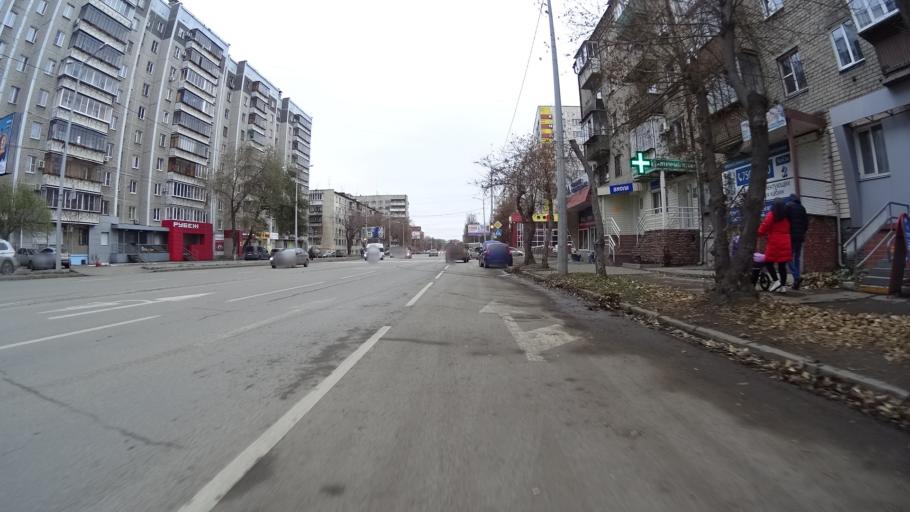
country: RU
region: Chelyabinsk
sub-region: Gorod Chelyabinsk
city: Chelyabinsk
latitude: 55.1567
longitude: 61.4174
